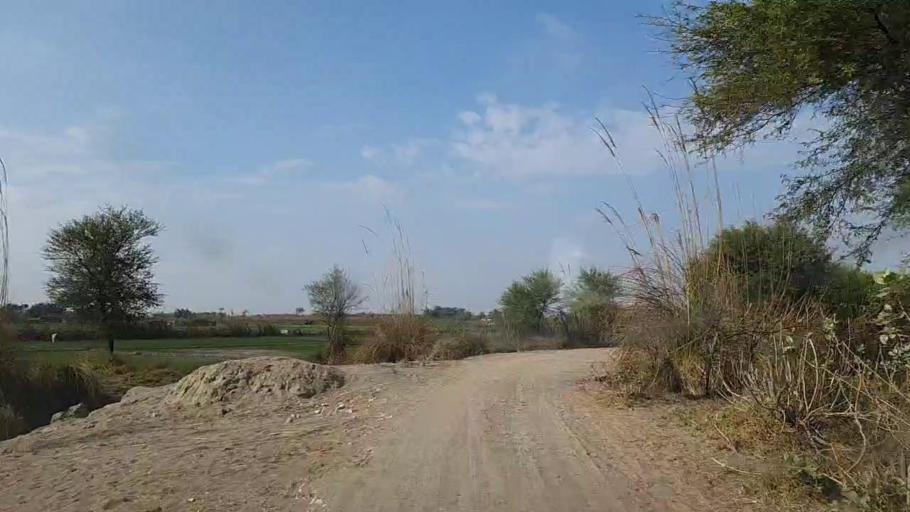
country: PK
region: Sindh
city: Sanghar
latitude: 26.2548
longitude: 69.0100
